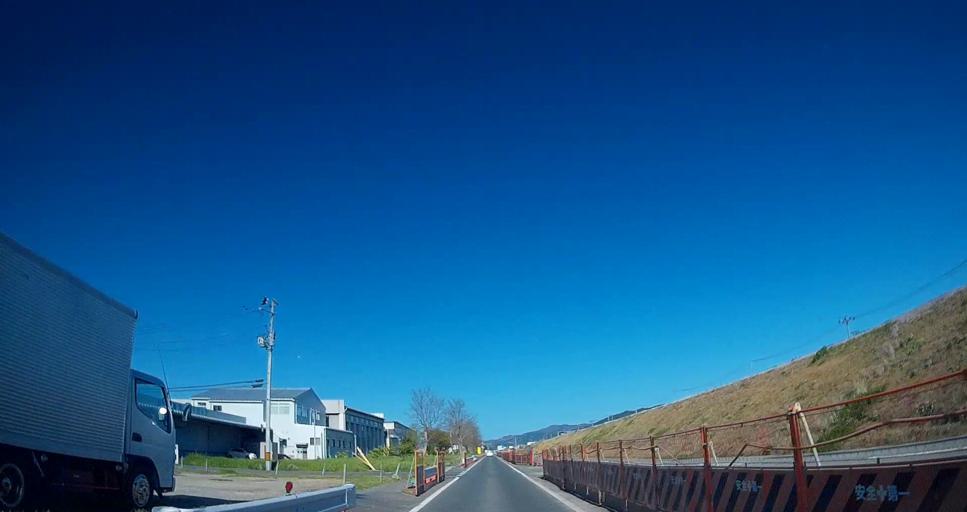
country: JP
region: Miyagi
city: Ishinomaki
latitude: 38.4160
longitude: 141.3274
